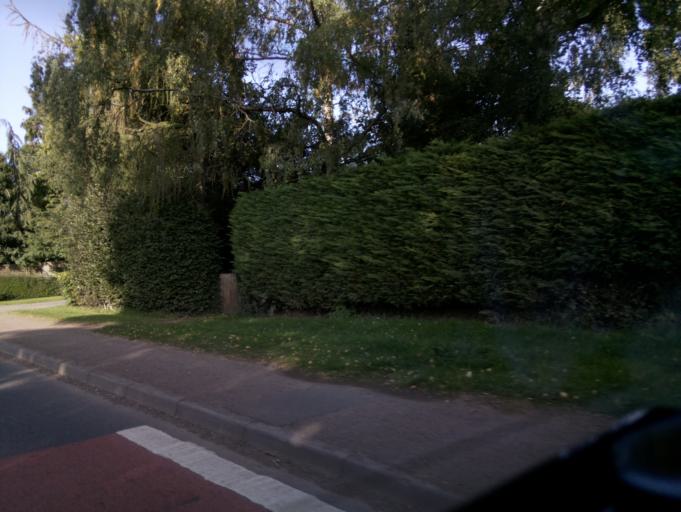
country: GB
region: England
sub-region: Gloucestershire
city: Newent
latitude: 51.9587
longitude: -2.3043
